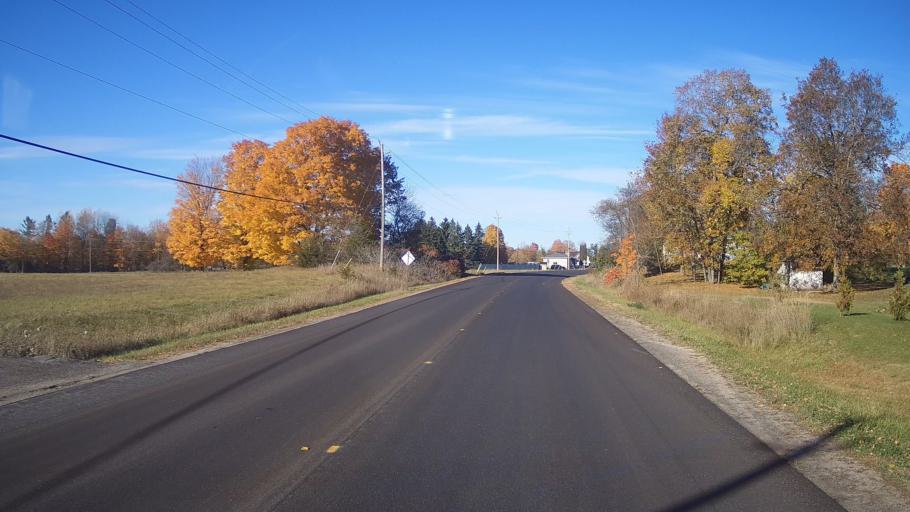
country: CA
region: Ontario
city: Kingston
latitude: 44.4680
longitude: -76.4922
